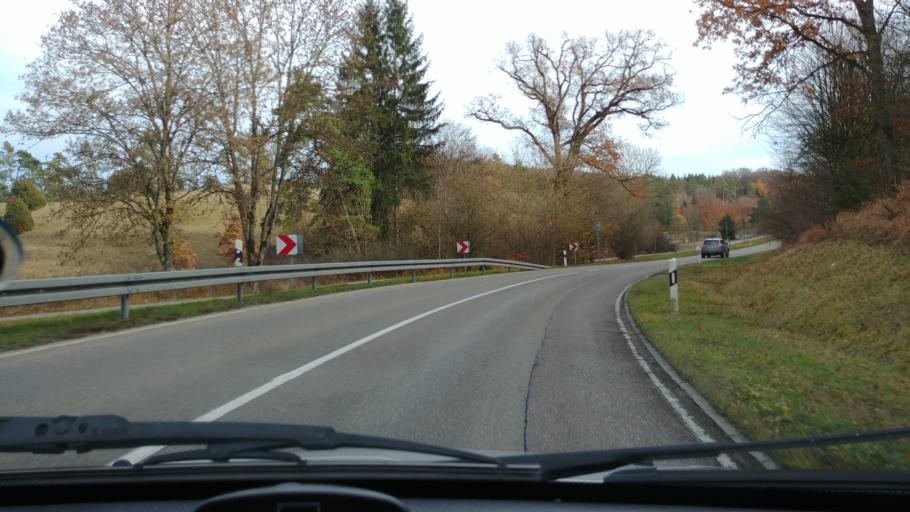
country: DE
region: Baden-Wuerttemberg
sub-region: Regierungsbezirk Stuttgart
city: Heidenheim an der Brenz
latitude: 48.6678
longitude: 10.1951
